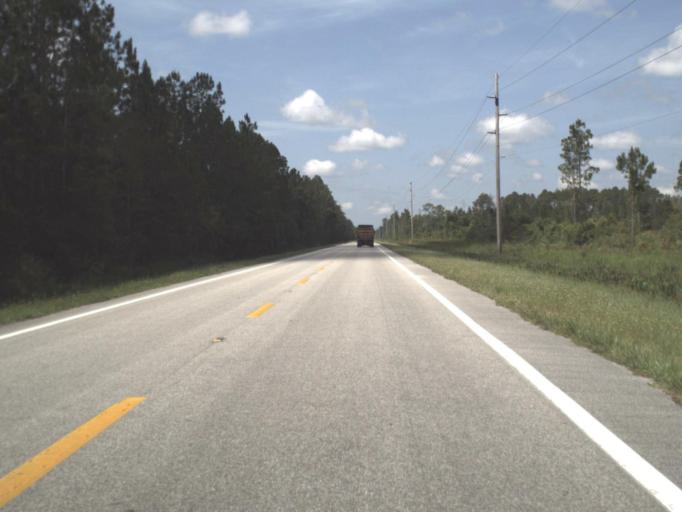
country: US
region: Florida
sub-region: Levy County
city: Bronson
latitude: 29.3994
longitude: -82.6944
